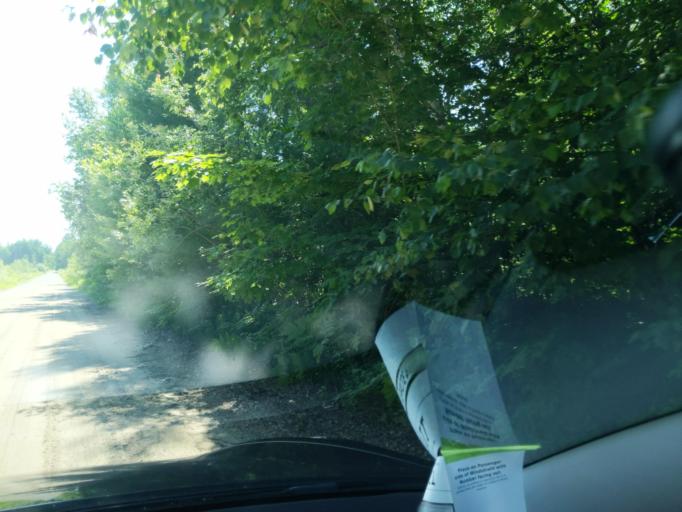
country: US
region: Michigan
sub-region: Cheboygan County
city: Cheboygan
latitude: 45.6792
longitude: -84.6619
